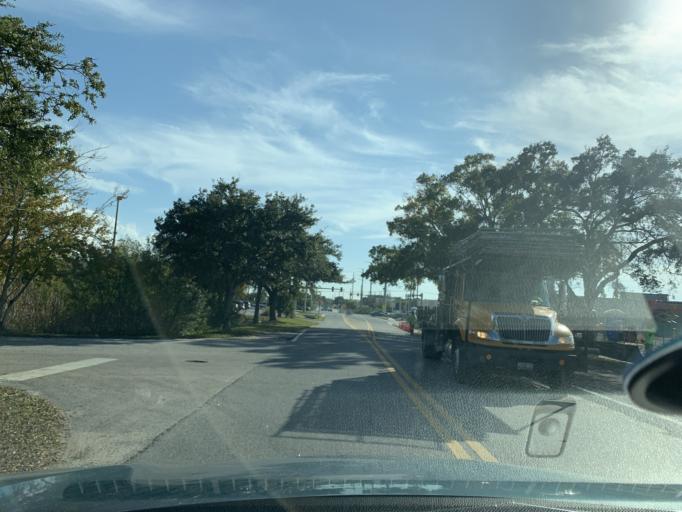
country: US
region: Florida
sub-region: Pinellas County
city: Largo
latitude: 27.8961
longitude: -82.7790
